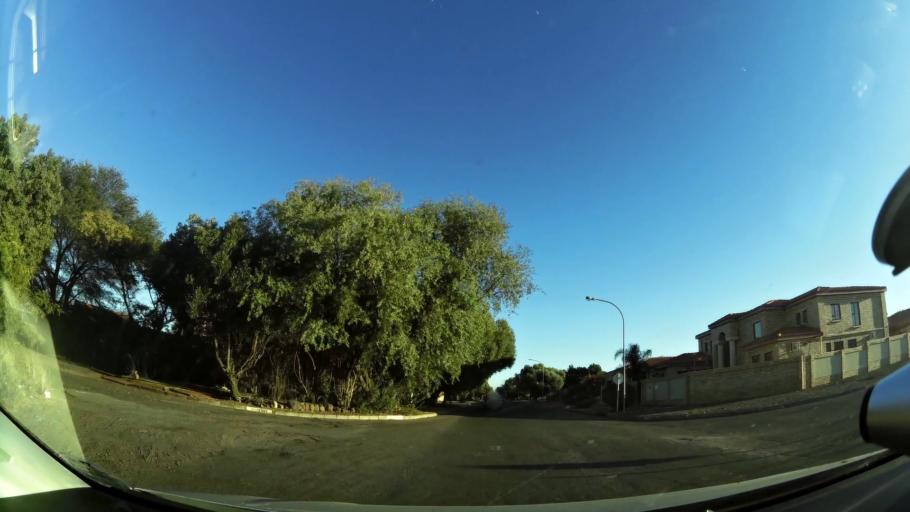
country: ZA
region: Northern Cape
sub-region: Frances Baard District Municipality
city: Kimberley
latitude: -28.7598
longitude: 24.7353
